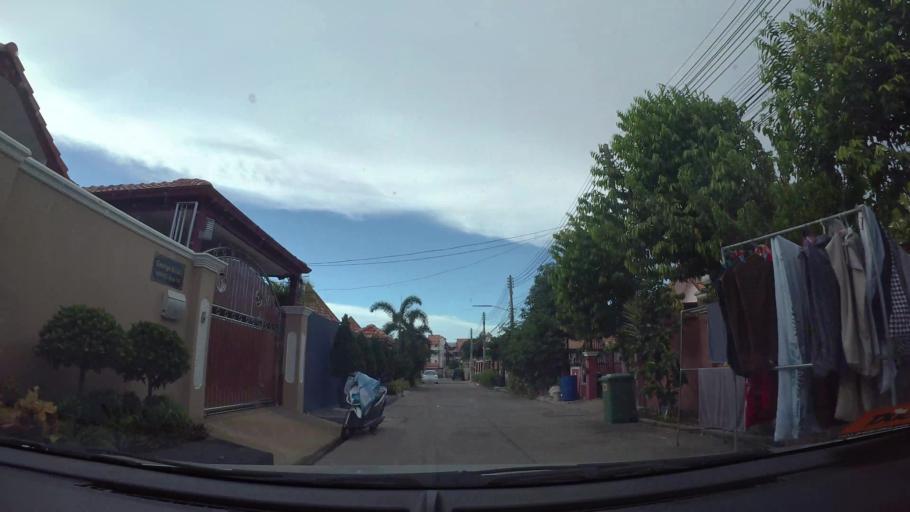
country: TH
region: Chon Buri
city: Phatthaya
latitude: 12.9130
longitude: 100.8757
